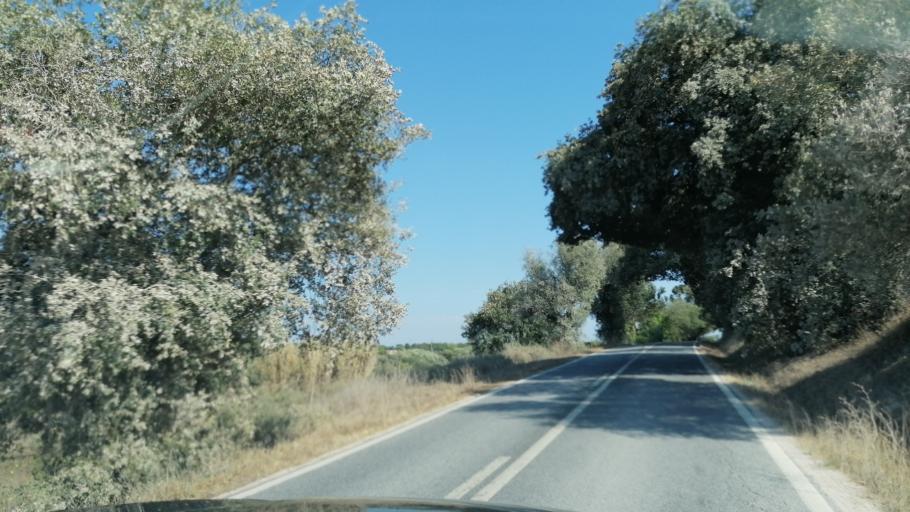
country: PT
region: Santarem
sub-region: Benavente
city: Poceirao
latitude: 38.7673
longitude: -8.6217
